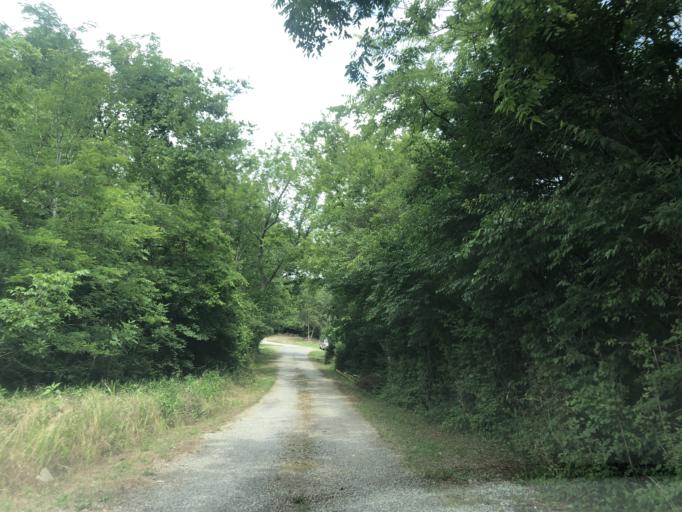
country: US
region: Tennessee
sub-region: Davidson County
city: Nashville
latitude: 36.2071
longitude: -86.8108
